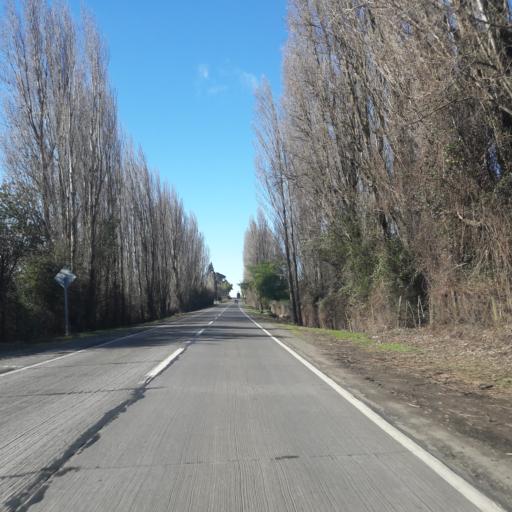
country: CL
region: Araucania
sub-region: Provincia de Malleco
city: Angol
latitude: -37.7639
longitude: -72.5642
